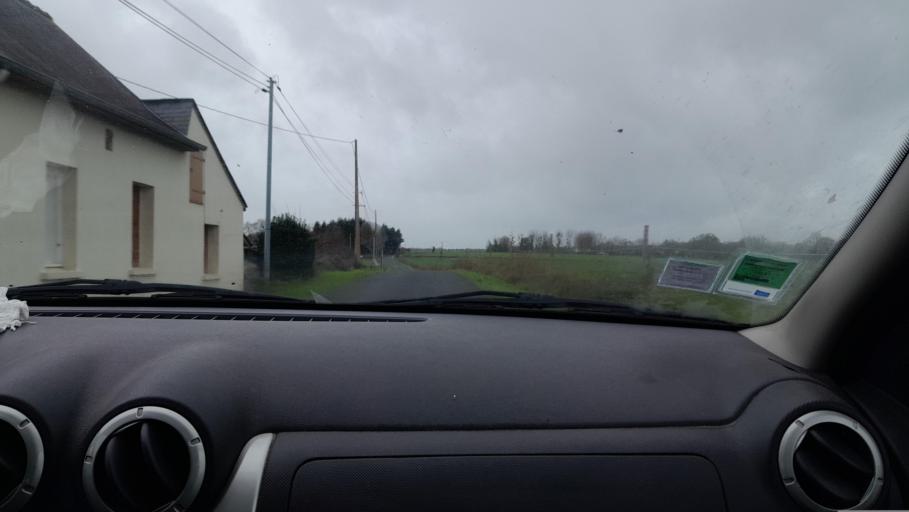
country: FR
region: Brittany
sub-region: Departement d'Ille-et-Vilaine
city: La Guerche-de-Bretagne
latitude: 47.9127
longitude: -1.1465
